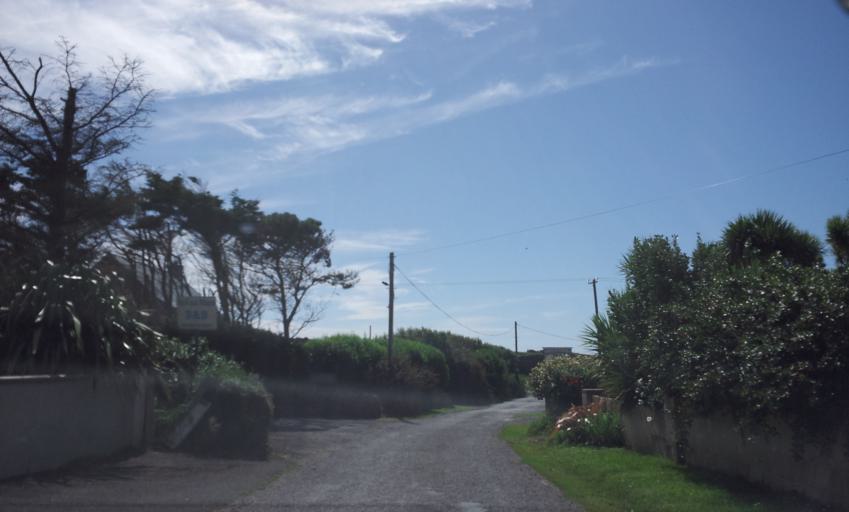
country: IE
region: Munster
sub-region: Ciarrai
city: Dingle
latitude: 52.1229
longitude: -10.3255
